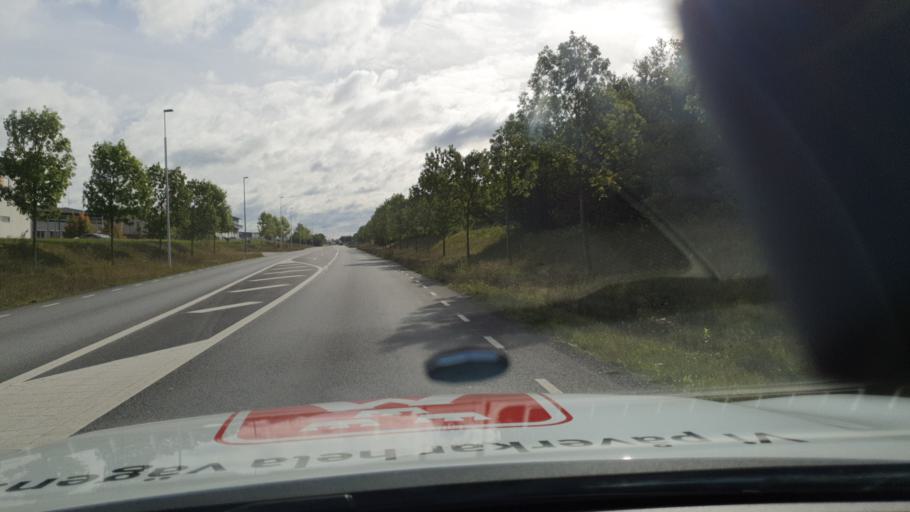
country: SE
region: Skane
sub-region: Malmo
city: Tygelsjo
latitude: 55.5568
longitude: 13.0279
